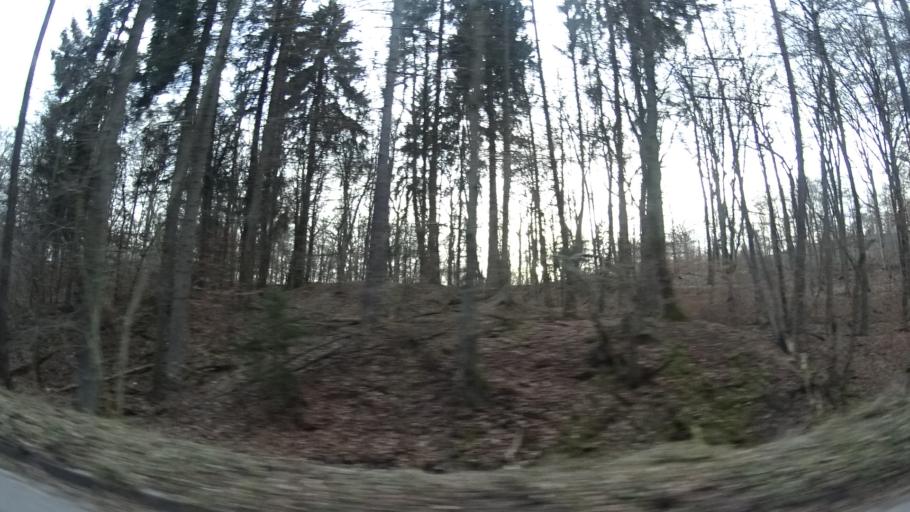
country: DE
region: Baden-Wuerttemberg
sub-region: Regierungsbezirk Stuttgart
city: Gerlingen
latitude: 48.7674
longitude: 9.0542
